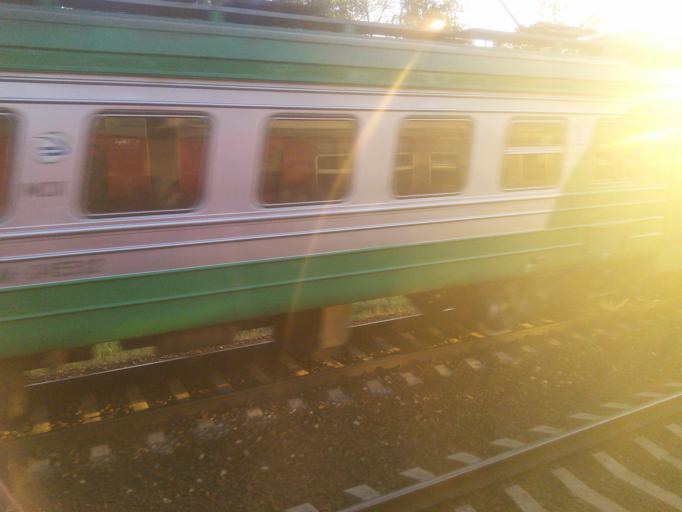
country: RU
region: Moskovskaya
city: Kupavna
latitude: 55.7478
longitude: 38.1412
